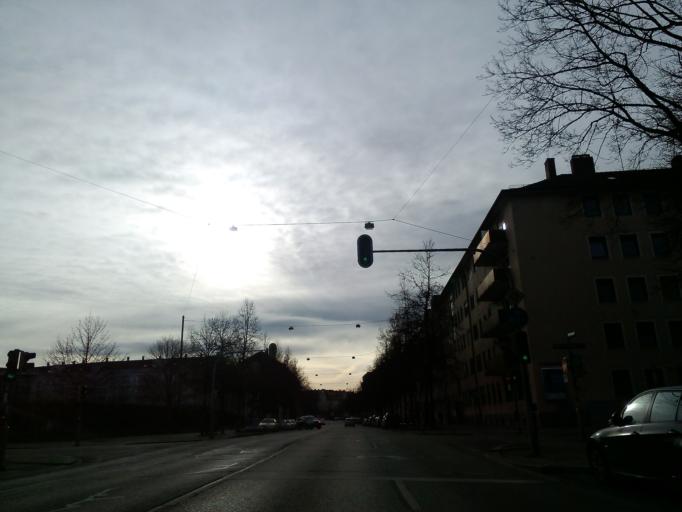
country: DE
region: Bavaria
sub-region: Upper Bavaria
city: Munich
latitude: 48.1161
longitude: 11.5482
